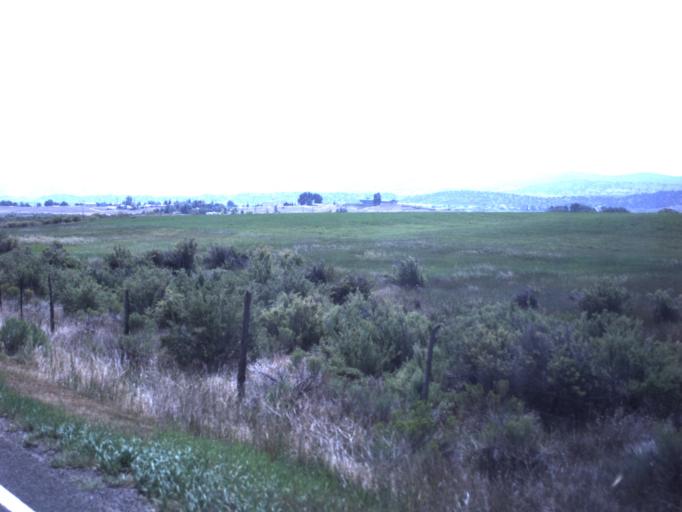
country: US
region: Utah
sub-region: Daggett County
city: Manila
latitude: 40.9886
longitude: -109.7056
